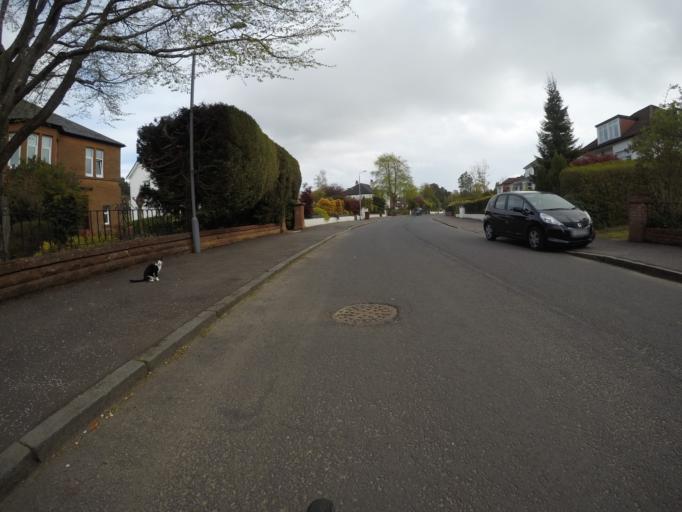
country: GB
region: Scotland
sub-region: East Renfrewshire
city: Giffnock
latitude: 55.7865
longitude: -4.3045
